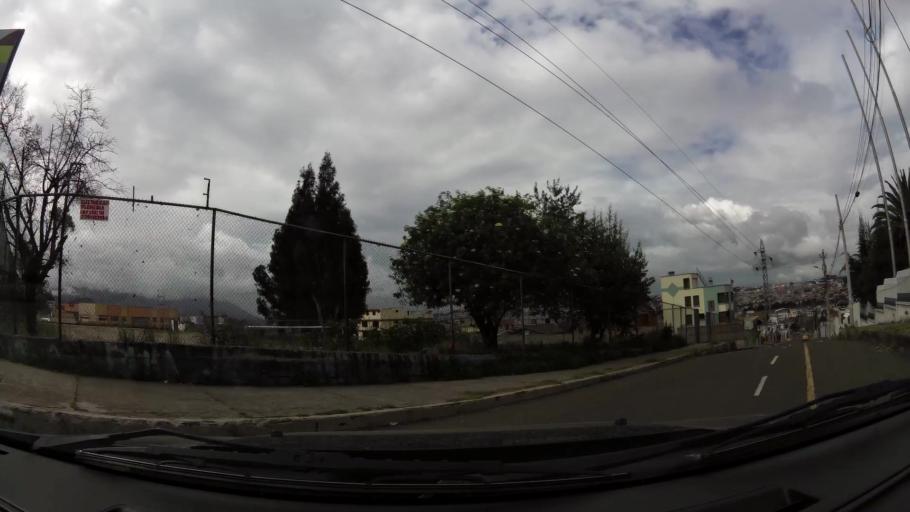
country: EC
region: Pichincha
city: Quito
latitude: -0.1421
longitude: -78.5004
